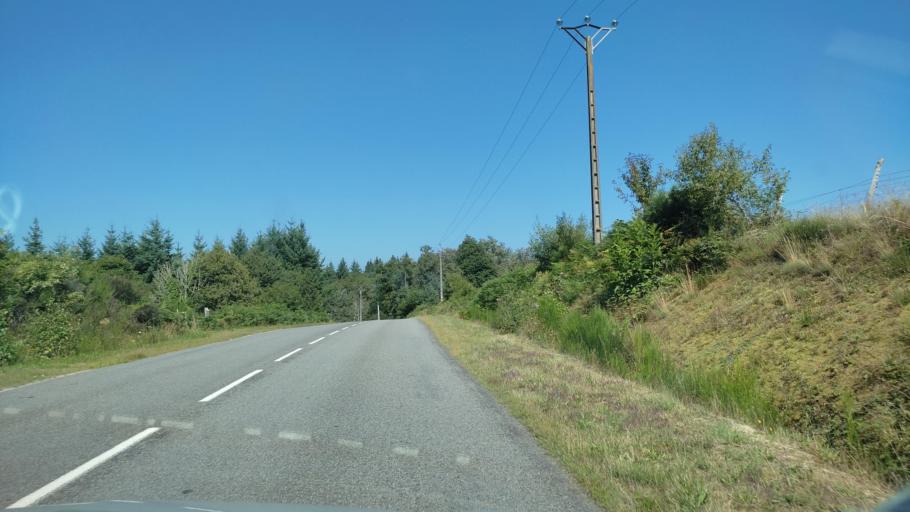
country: FR
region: Limousin
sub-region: Departement de la Haute-Vienne
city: Razes
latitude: 46.0353
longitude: 1.3236
